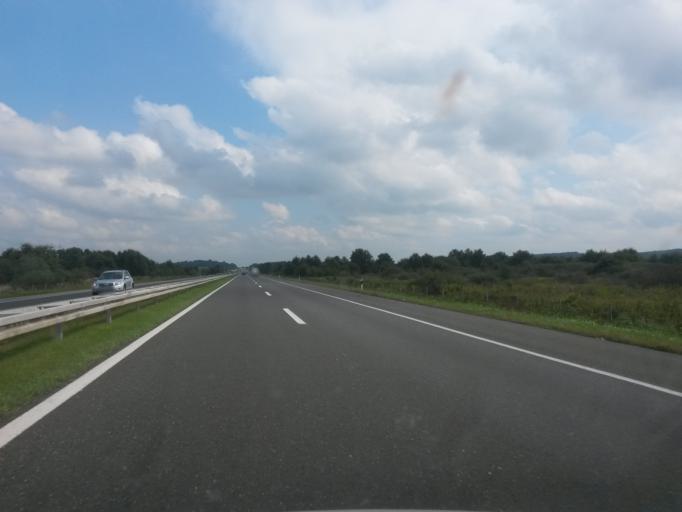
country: HR
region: Zagrebacka
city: Brckovljani
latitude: 45.8825
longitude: 16.2248
